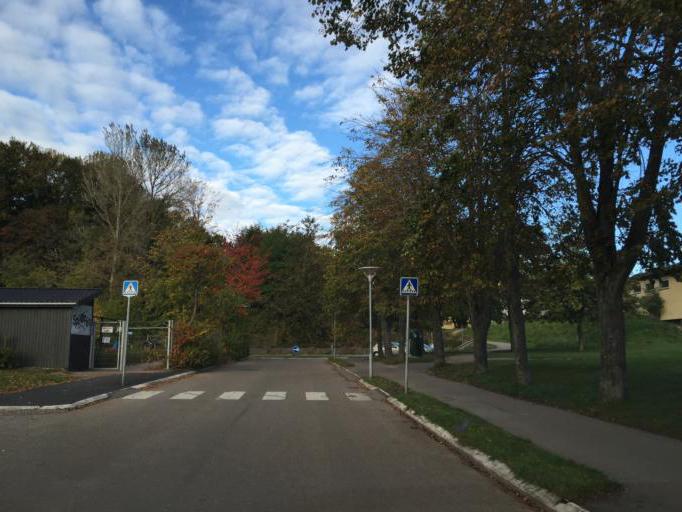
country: DK
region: Zealand
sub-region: Odsherred Kommune
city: Asnaes
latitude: 55.8136
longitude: 11.5003
